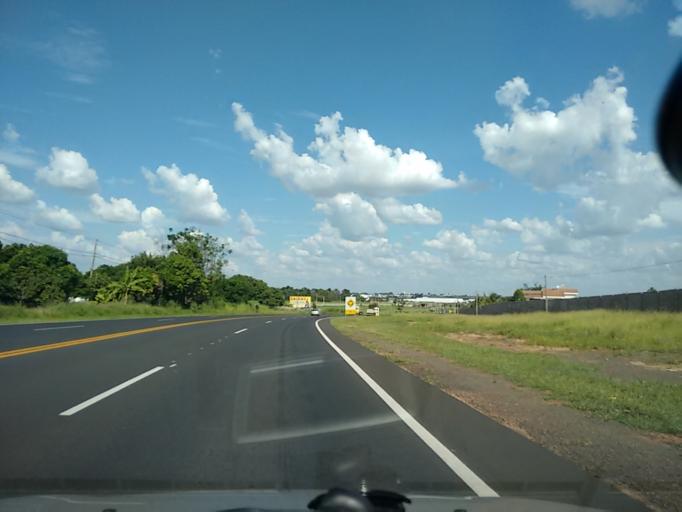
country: BR
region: Sao Paulo
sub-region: Marilia
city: Marilia
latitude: -22.1575
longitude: -50.0020
